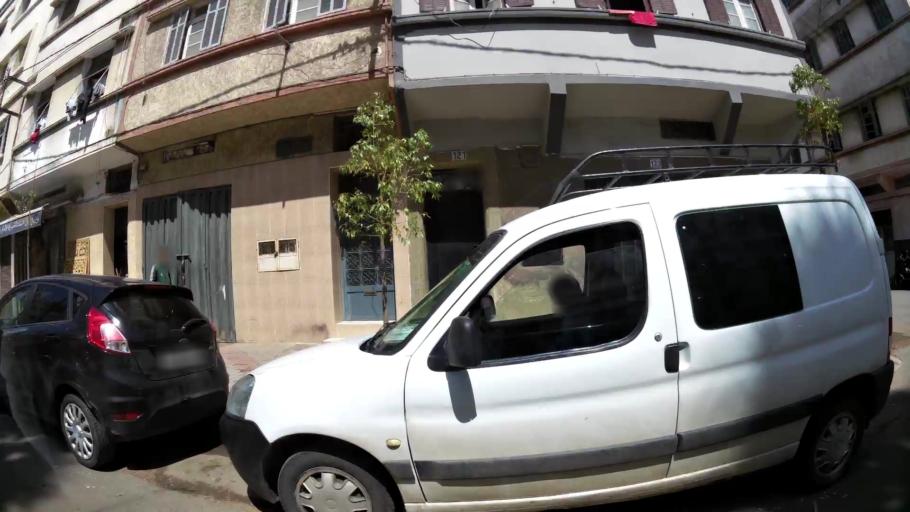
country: MA
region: Grand Casablanca
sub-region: Casablanca
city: Casablanca
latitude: 33.5601
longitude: -7.5980
